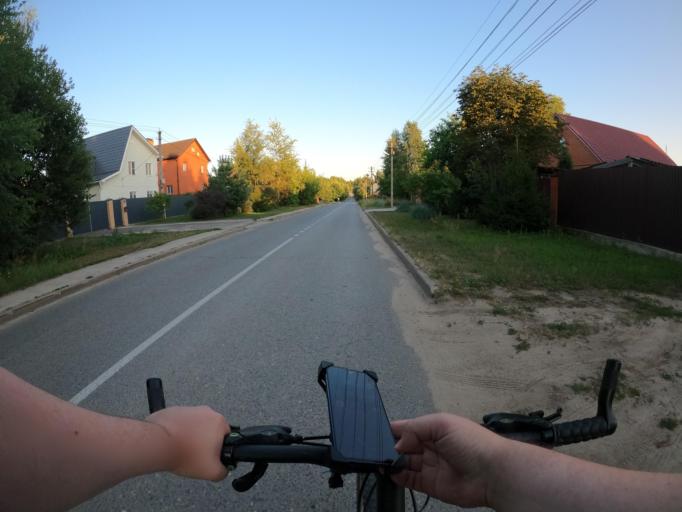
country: RU
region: Moskovskaya
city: Beloozerskiy
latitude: 55.4648
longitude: 38.4299
